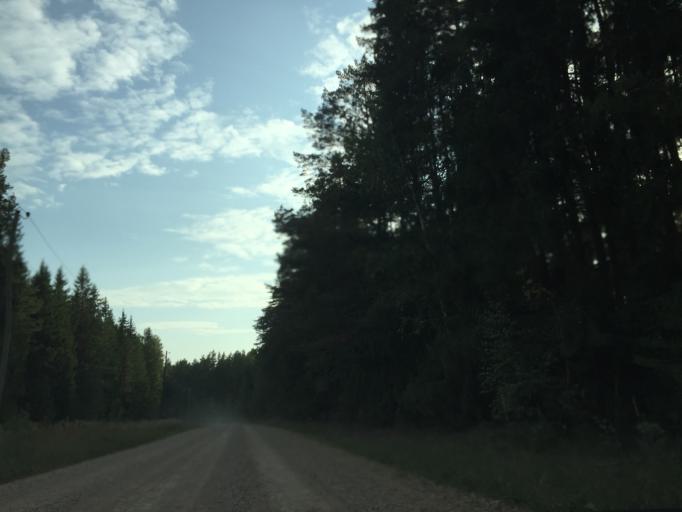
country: LV
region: Ikskile
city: Ikskile
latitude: 56.8018
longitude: 24.4393
